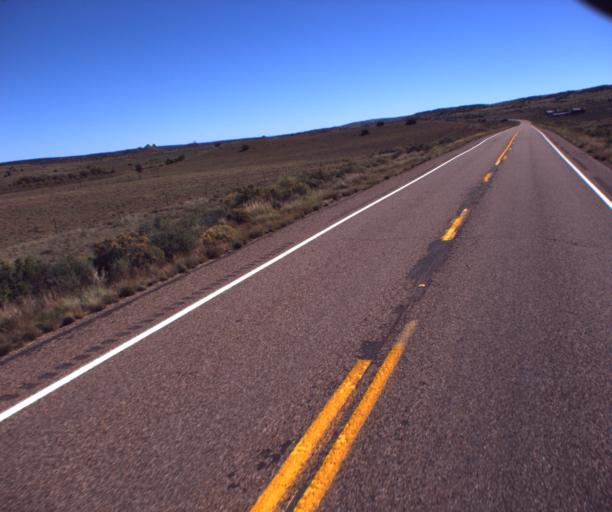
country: US
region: Arizona
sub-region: Apache County
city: Saint Johns
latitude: 34.5873
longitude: -109.5869
